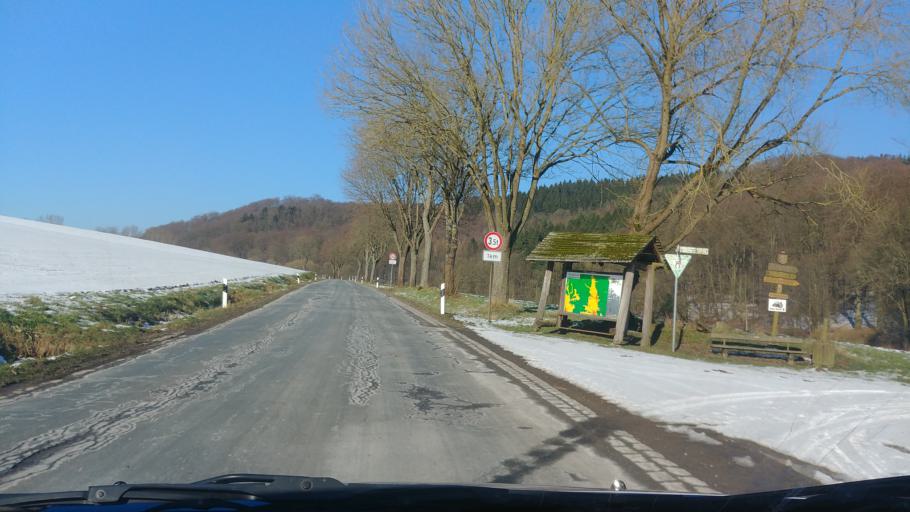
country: DE
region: Lower Saxony
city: Hardegsen
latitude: 51.6878
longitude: 9.7420
